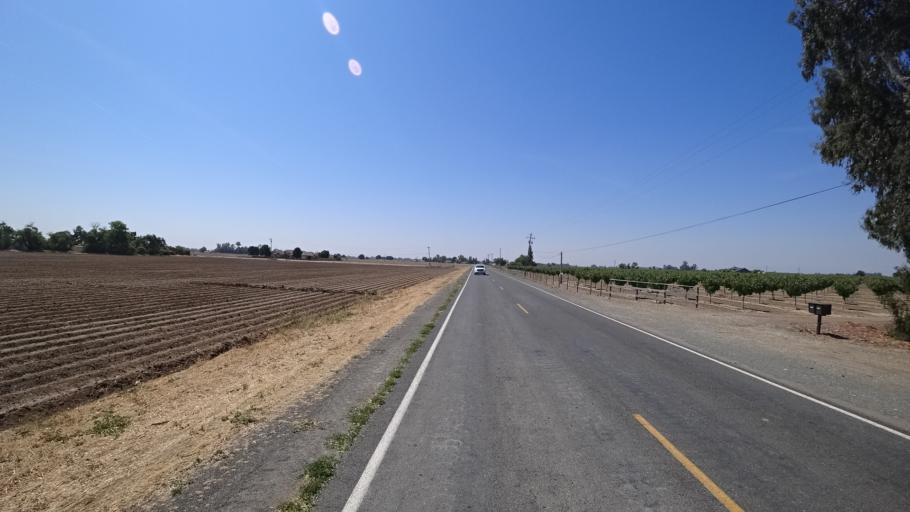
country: US
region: California
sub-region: Fresno County
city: Riverdale
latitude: 36.3818
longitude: -119.8513
